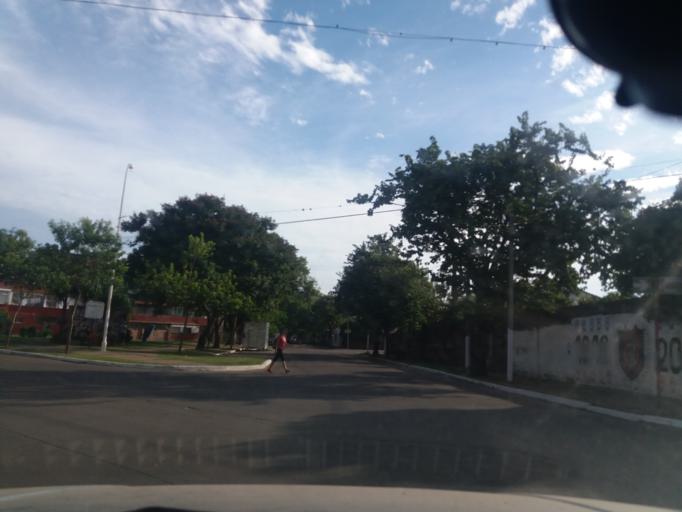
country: AR
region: Corrientes
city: Corrientes
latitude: -27.4832
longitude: -58.8308
